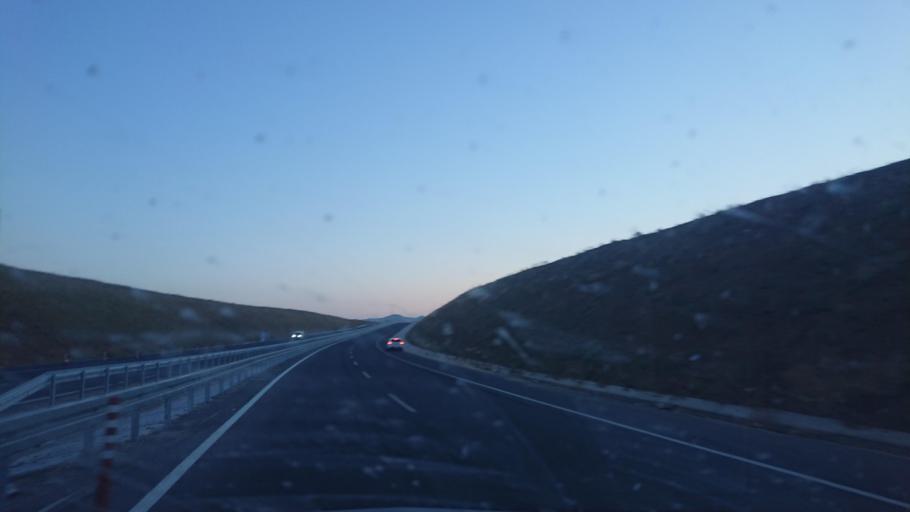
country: TR
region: Aksaray
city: Balci
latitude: 38.7816
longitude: 34.1167
